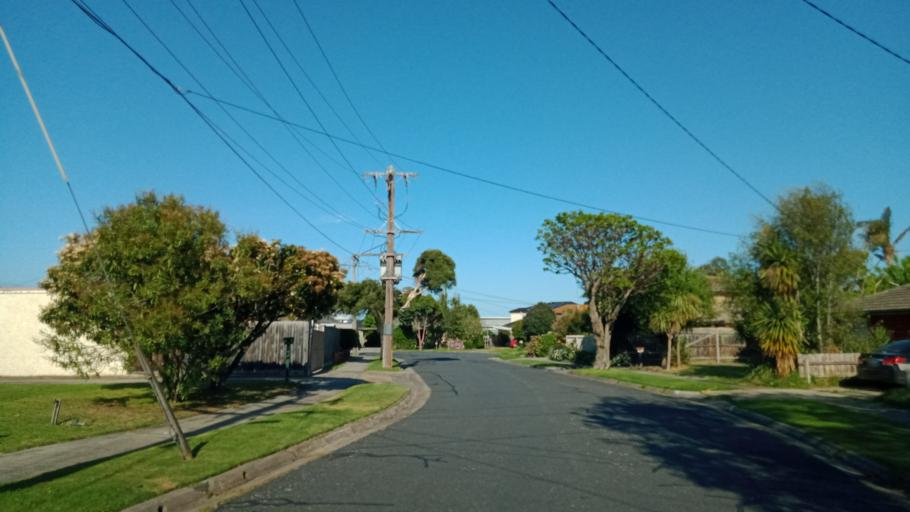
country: AU
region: Victoria
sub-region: Kingston
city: Chelsea Heights
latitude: -38.0414
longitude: 145.1314
